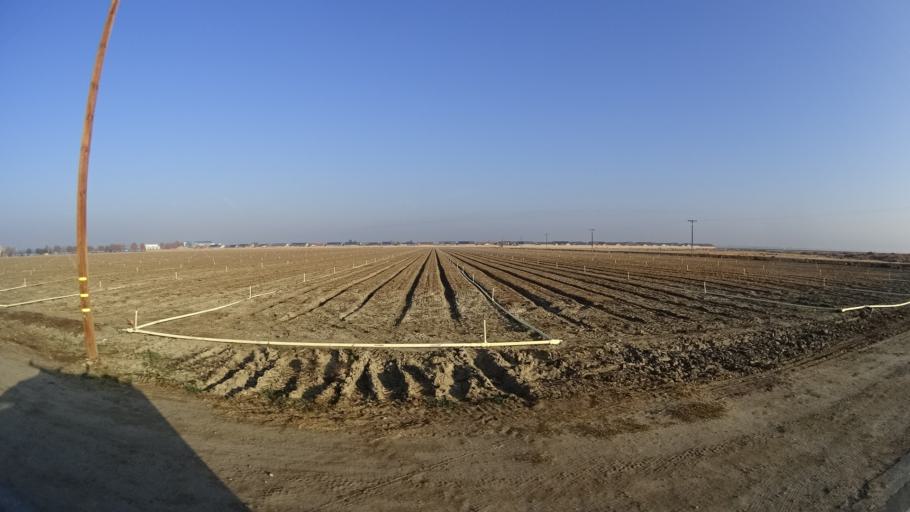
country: US
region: California
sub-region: Kern County
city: Greenacres
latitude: 35.2817
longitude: -119.1059
